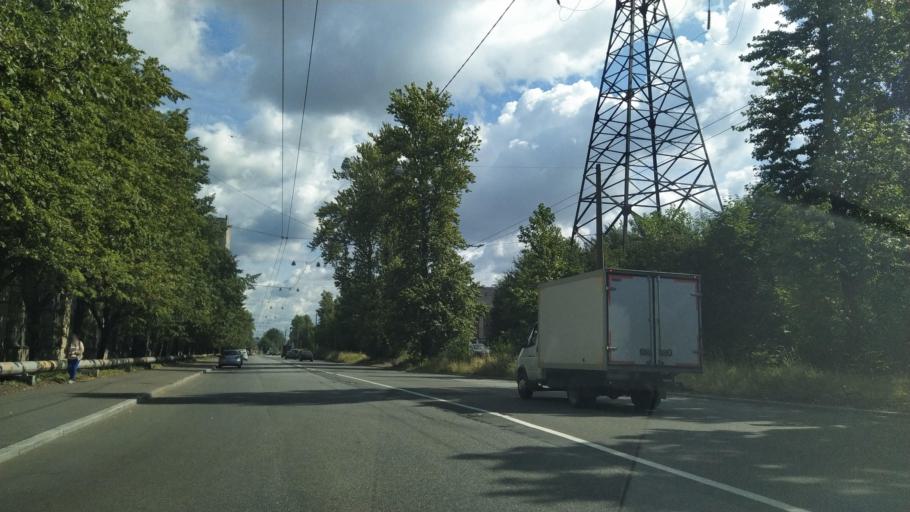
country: RU
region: Leningrad
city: Finlyandskiy
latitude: 59.9698
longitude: 30.3575
